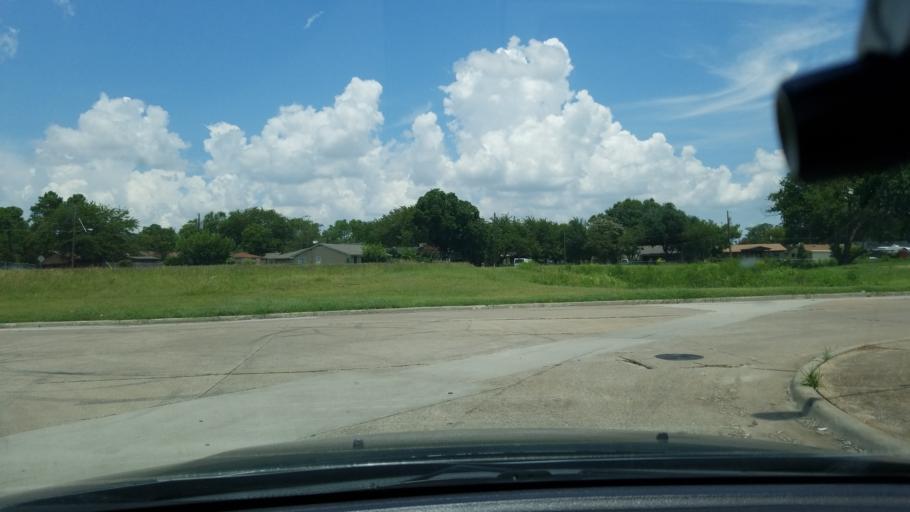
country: US
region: Texas
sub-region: Dallas County
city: Balch Springs
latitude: 32.7423
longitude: -96.6520
